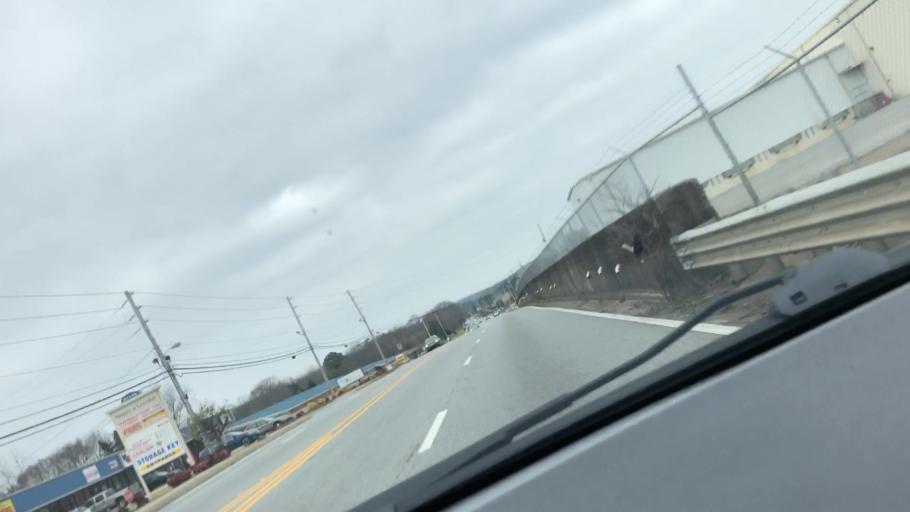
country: US
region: Georgia
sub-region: Bartow County
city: Cartersville
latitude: 34.2086
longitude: -84.8192
